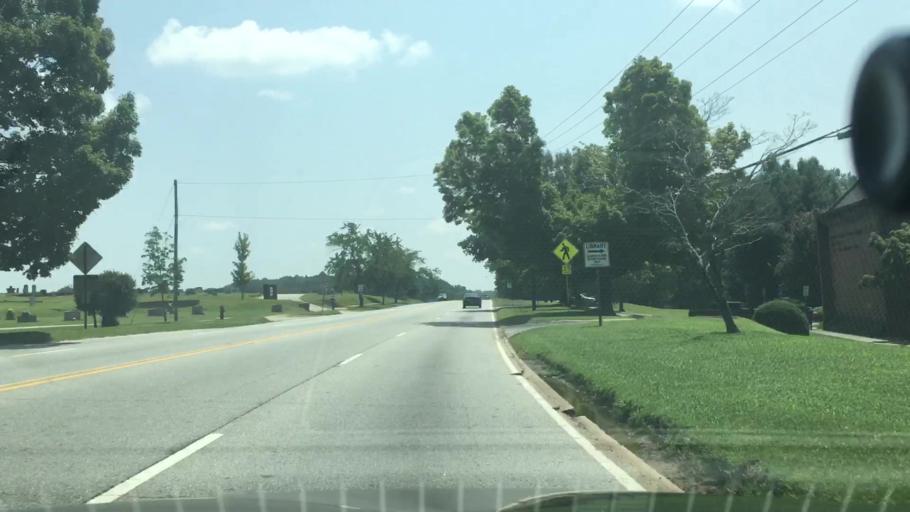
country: US
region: Georgia
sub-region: Spalding County
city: Griffin
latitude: 33.2458
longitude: -84.2534
